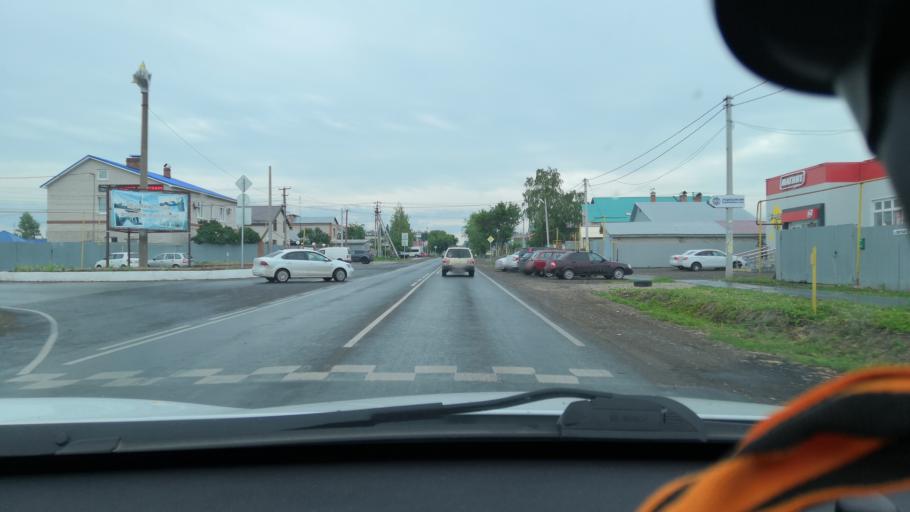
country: RU
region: Samara
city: Novosemeykino
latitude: 53.3756
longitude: 50.3470
